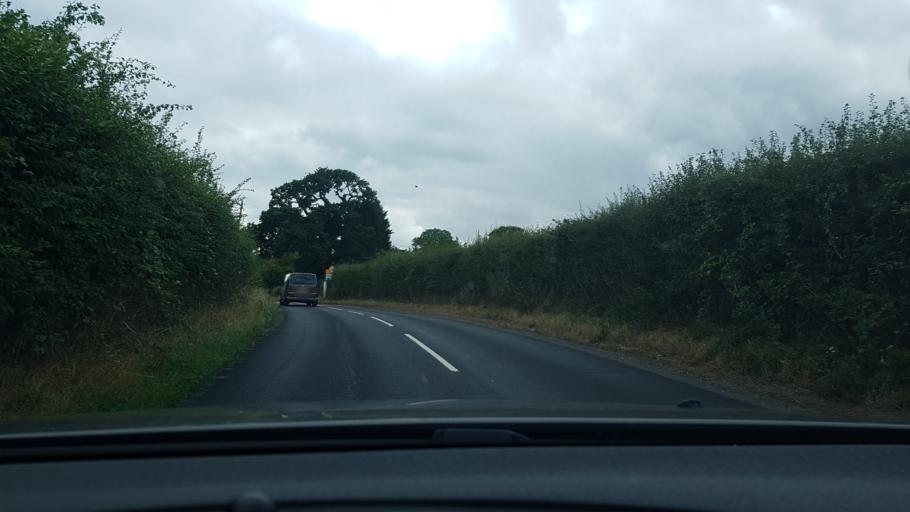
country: GB
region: England
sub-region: West Berkshire
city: Theale
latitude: 51.4470
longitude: -1.1233
